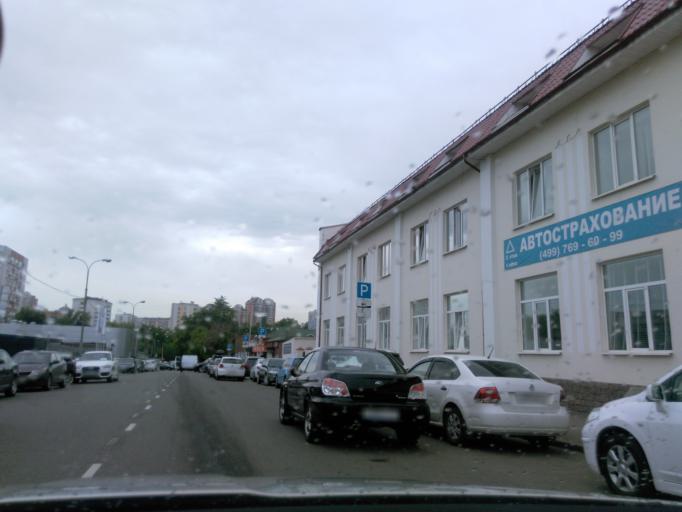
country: RU
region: Moscow
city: Taganskiy
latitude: 55.7306
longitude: 37.6856
